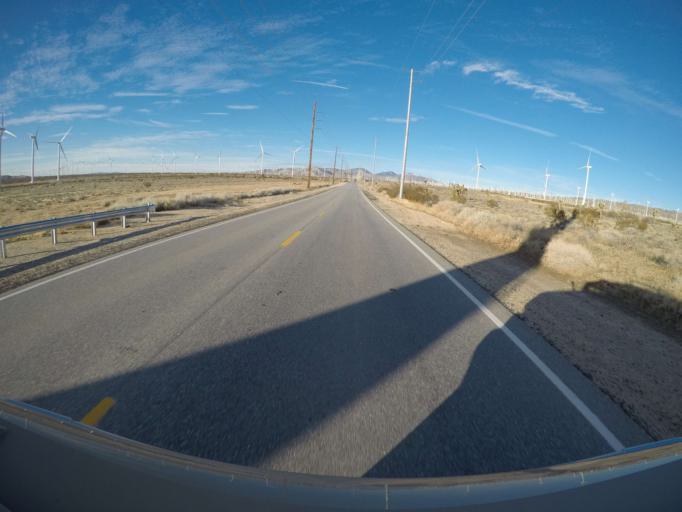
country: US
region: California
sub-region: Kern County
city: Mojave
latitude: 35.0401
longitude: -118.2446
